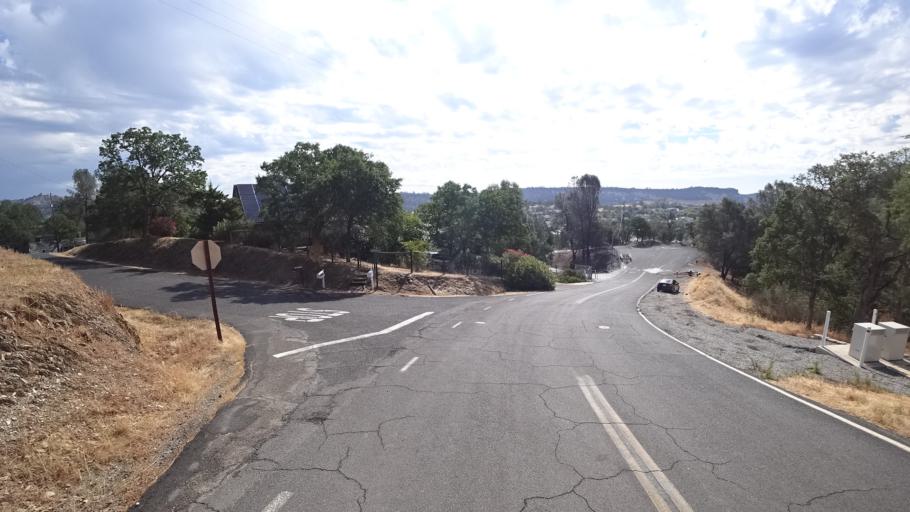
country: US
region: California
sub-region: Calaveras County
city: Copperopolis
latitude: 37.9121
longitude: -120.6057
